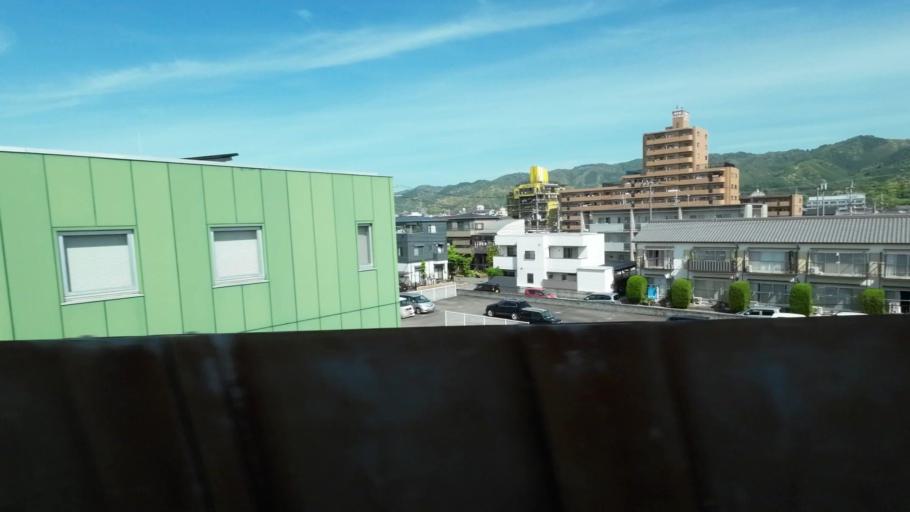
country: JP
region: Kochi
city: Kochi-shi
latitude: 33.5684
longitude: 133.5518
